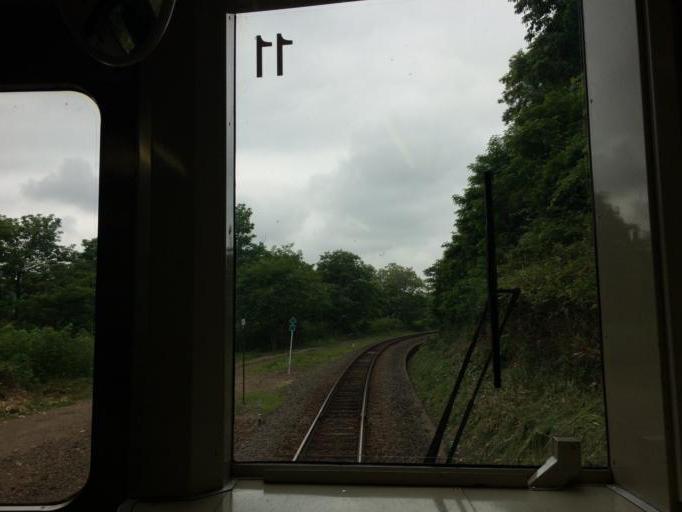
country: JP
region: Hokkaido
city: Iwanai
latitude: 42.9731
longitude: 140.6751
